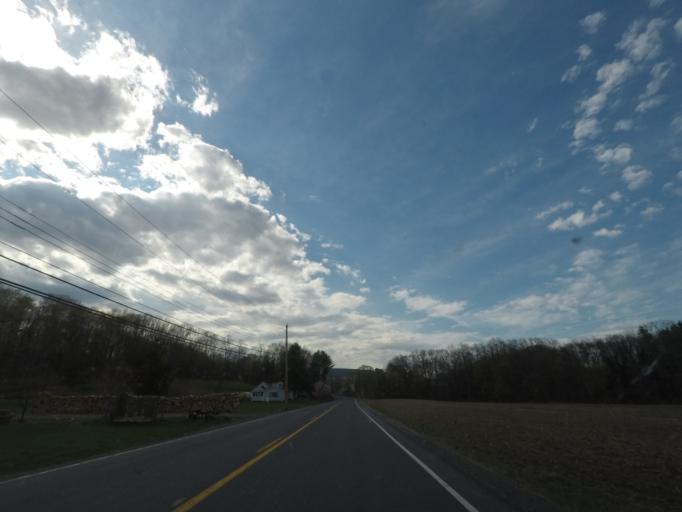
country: US
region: New York
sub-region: Albany County
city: Voorheesville
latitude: 42.5721
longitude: -73.9568
